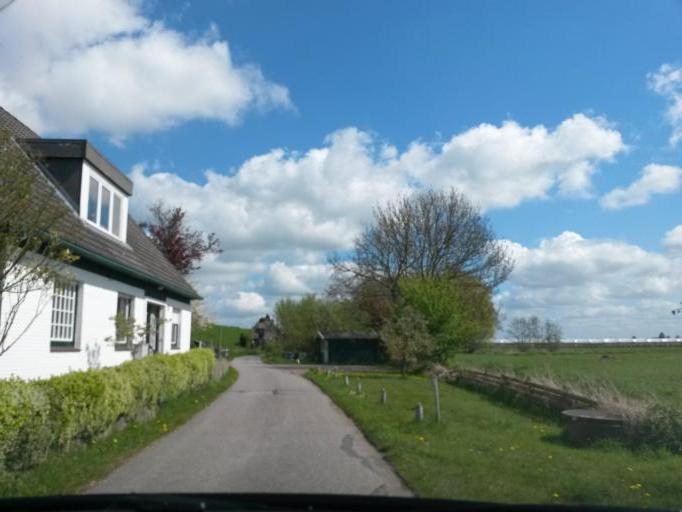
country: DE
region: Schleswig-Holstein
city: Seestermuhe
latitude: 53.6646
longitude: 9.5694
